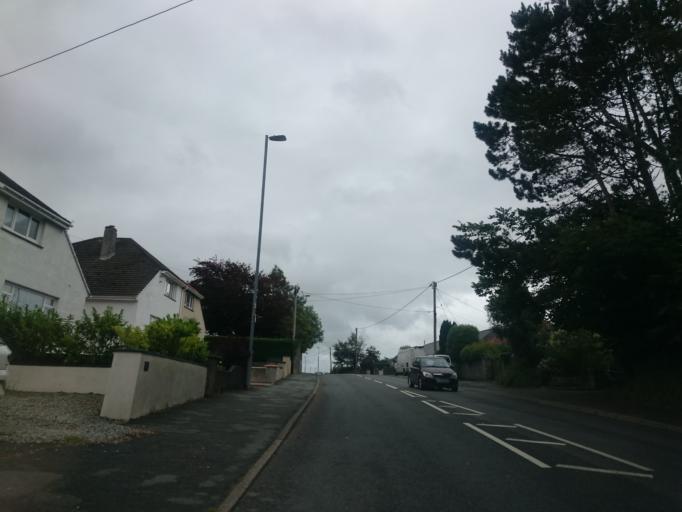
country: GB
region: Wales
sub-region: Pembrokeshire
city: Haverfordwest
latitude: 51.7872
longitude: -4.9751
